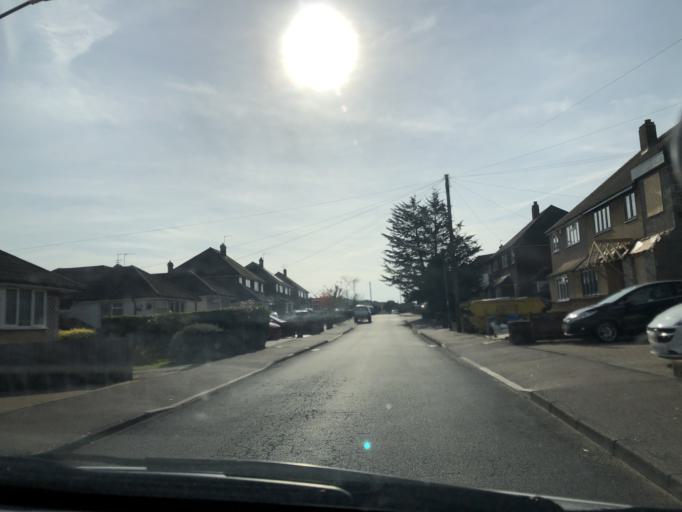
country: GB
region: England
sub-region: Kent
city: Dartford
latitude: 51.4315
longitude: 0.1887
